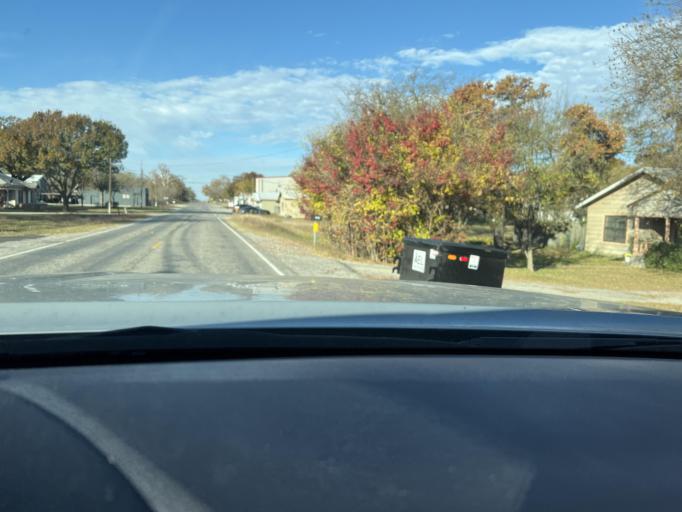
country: US
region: Texas
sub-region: Eastland County
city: Eastland
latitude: 32.4193
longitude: -98.7496
